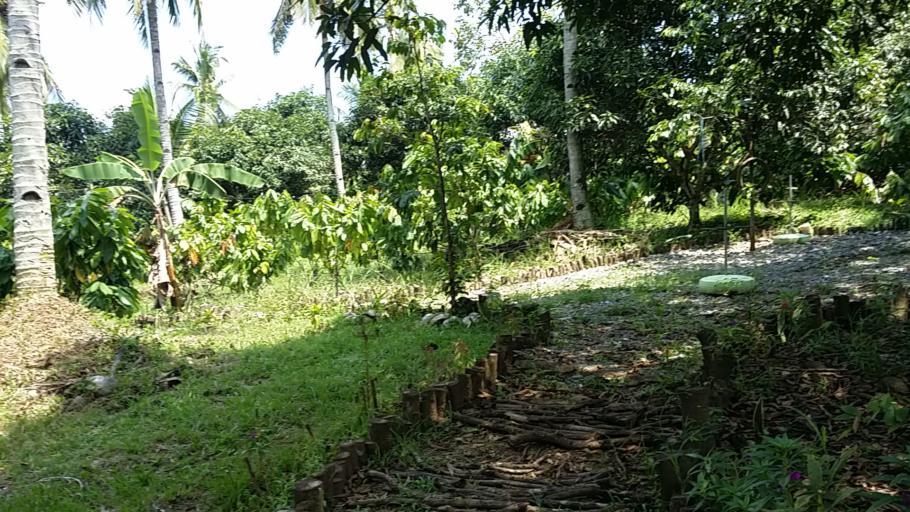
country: PH
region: Davao
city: Lacson
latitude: 7.2131
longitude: 125.4327
